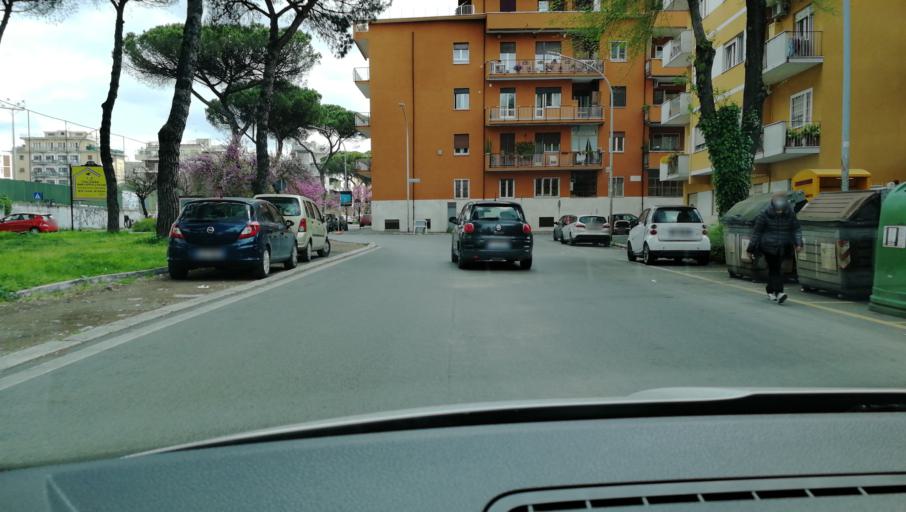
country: IT
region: Latium
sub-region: Citta metropolitana di Roma Capitale
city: Rome
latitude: 41.8516
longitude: 12.4988
